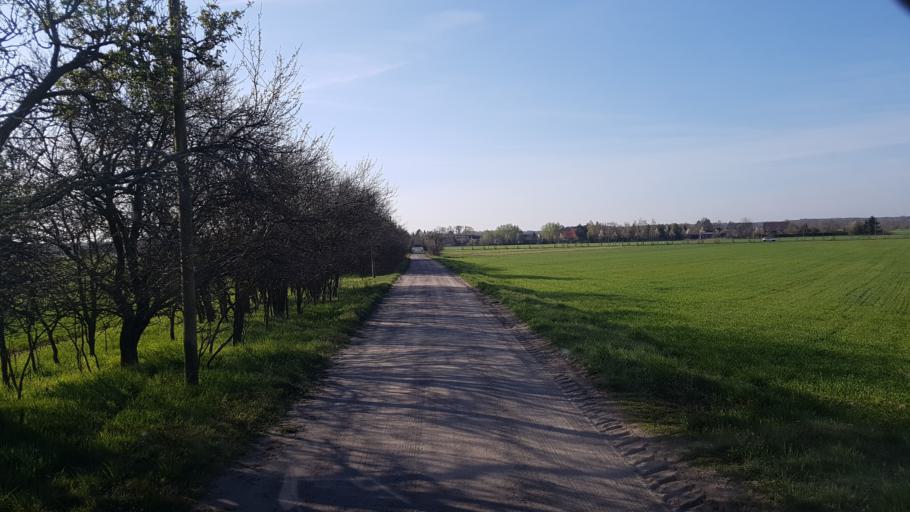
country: DE
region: Brandenburg
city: Doberlug-Kirchhain
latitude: 51.6178
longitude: 13.5861
